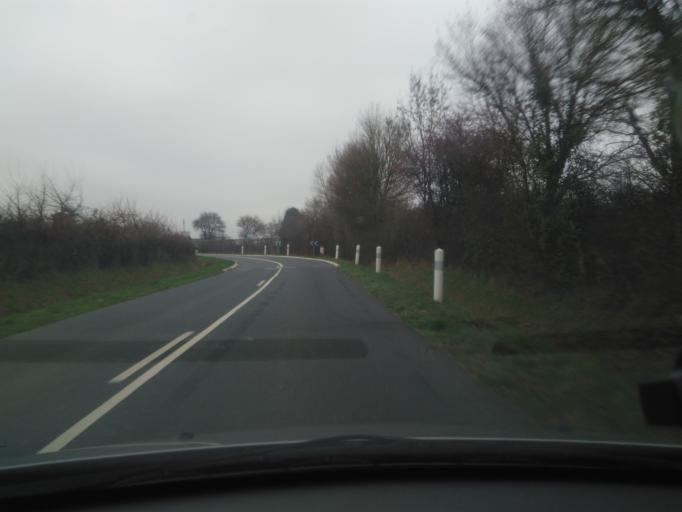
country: FR
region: Centre
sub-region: Departement de l'Indre
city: Montgivray
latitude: 46.6390
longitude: 2.0771
